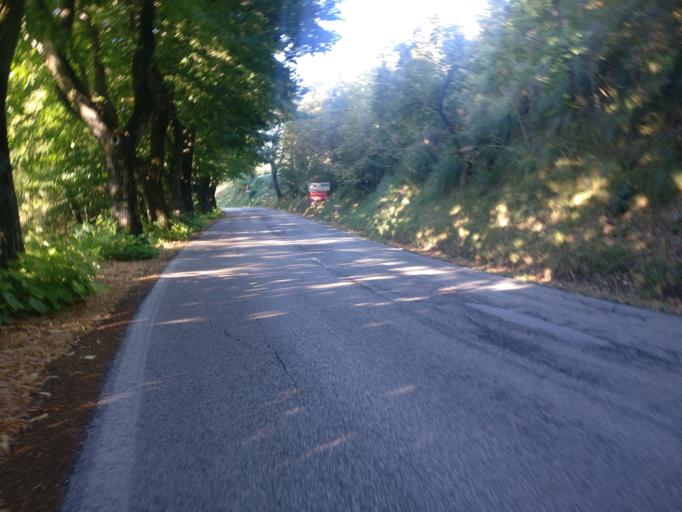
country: IT
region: The Marches
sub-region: Provincia di Ascoli Piceno
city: Montedinove
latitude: 42.9789
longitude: 13.5960
